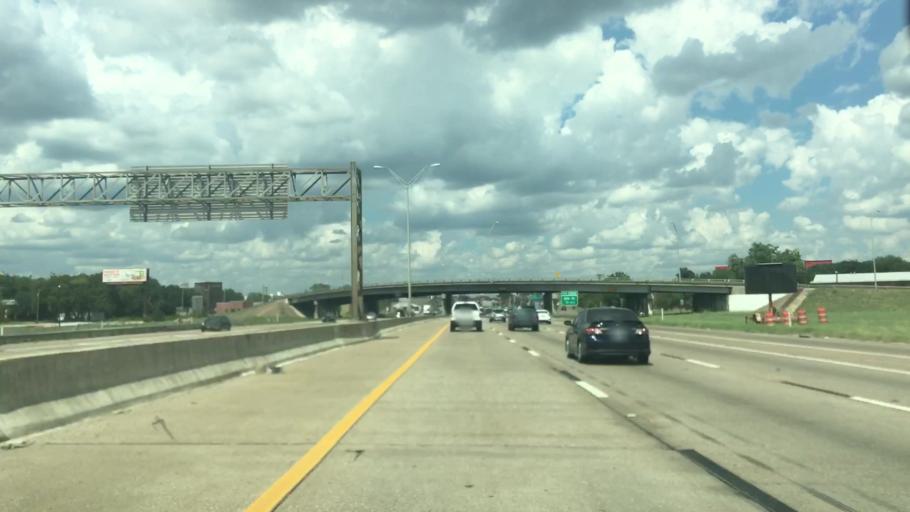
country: US
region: Texas
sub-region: McLennan County
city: Waco
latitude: 31.5406
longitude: -97.1280
